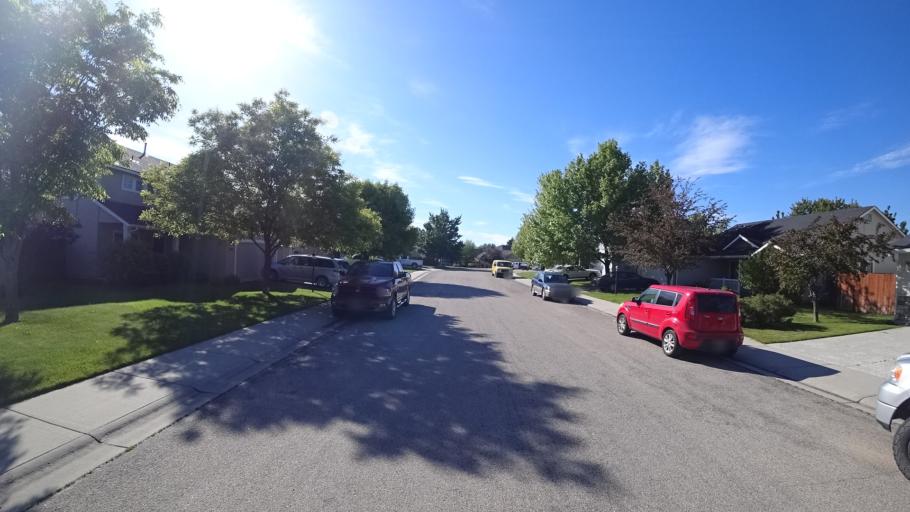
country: US
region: Idaho
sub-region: Ada County
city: Garden City
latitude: 43.5693
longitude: -116.2769
